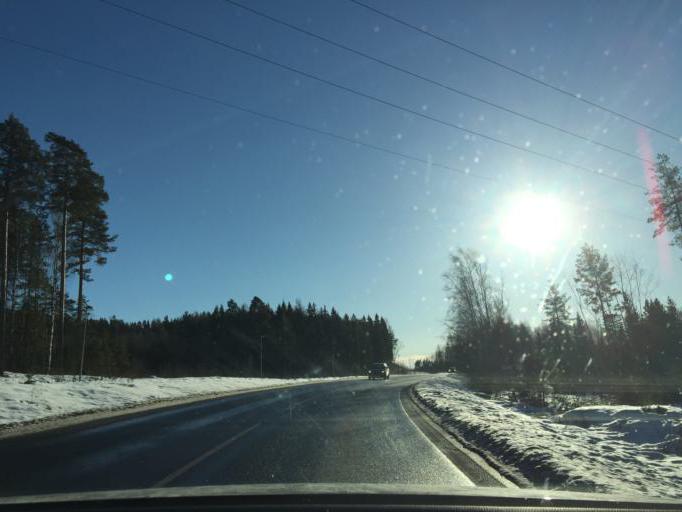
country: NO
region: Akershus
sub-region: Nes
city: Arnes
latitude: 60.1818
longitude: 11.5342
